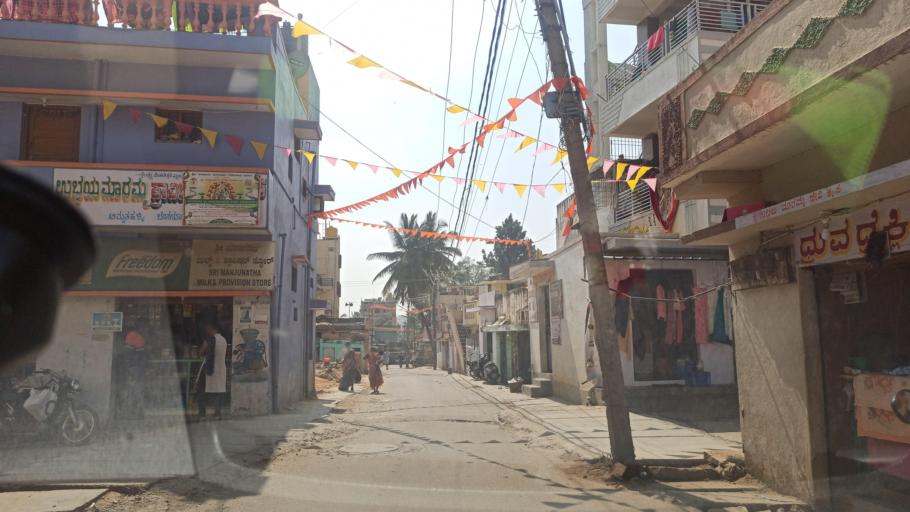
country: IN
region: Karnataka
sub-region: Bangalore Urban
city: Yelahanka
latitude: 13.0651
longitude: 77.6009
